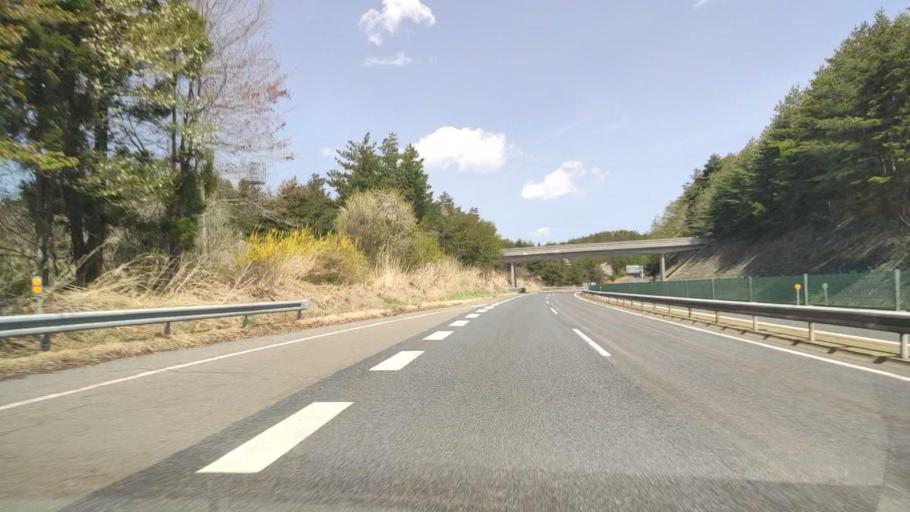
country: JP
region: Iwate
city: Ichinohe
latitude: 40.3003
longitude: 141.4231
